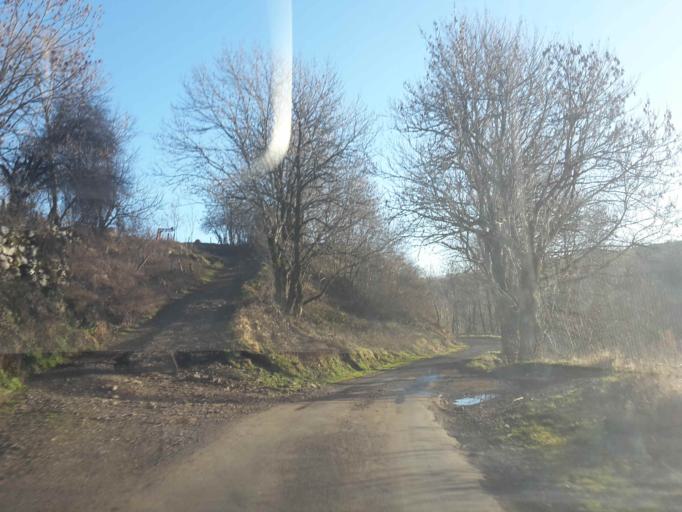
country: FR
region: Auvergne
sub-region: Departement du Cantal
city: Ydes
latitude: 45.2409
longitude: 2.5423
